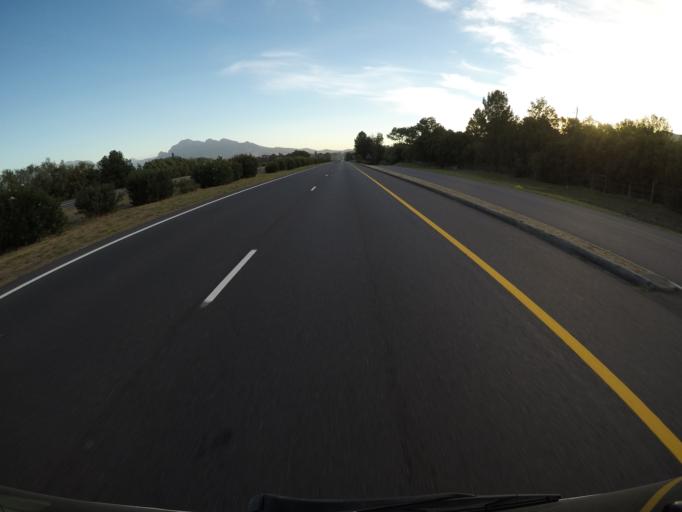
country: ZA
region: Western Cape
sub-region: Cape Winelands District Municipality
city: Paarl
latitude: -33.7553
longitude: 18.9857
